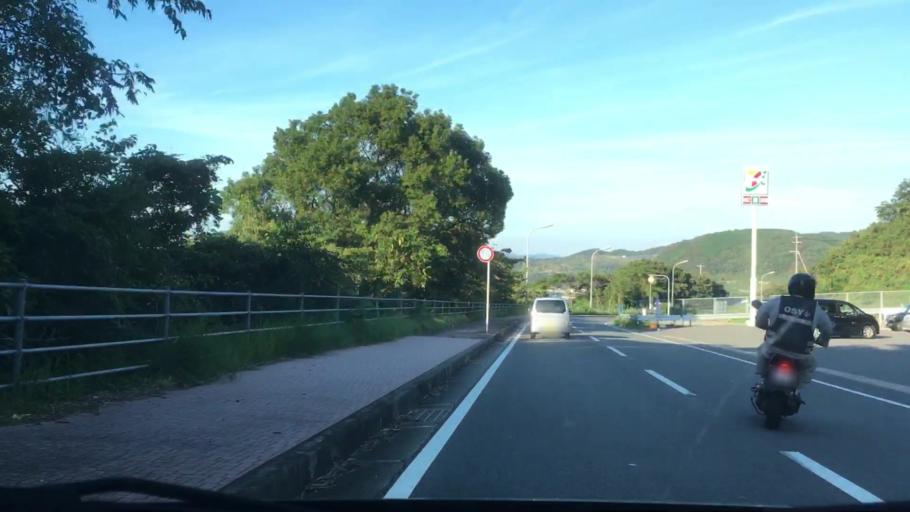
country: JP
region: Nagasaki
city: Sasebo
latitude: 33.0393
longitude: 129.6502
